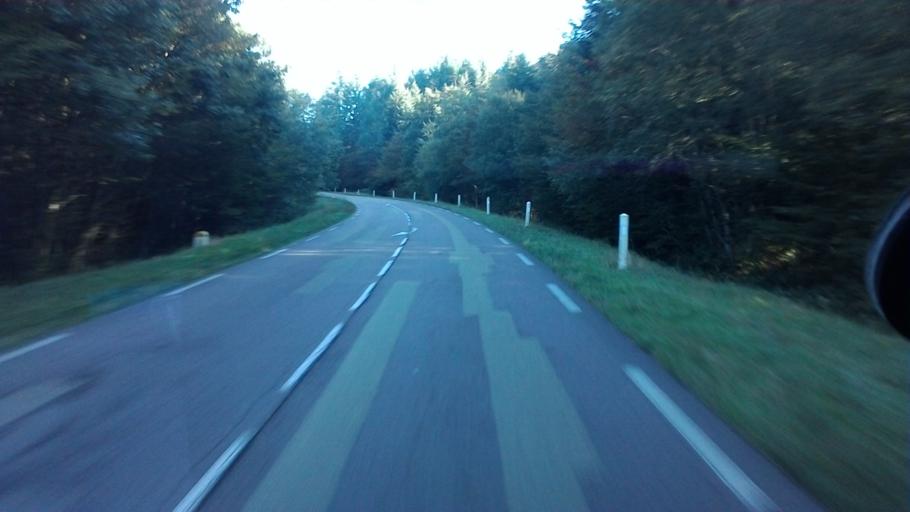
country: FR
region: Bourgogne
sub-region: Departement de la Cote-d'Or
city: Saulieu
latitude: 47.3257
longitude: 4.2716
